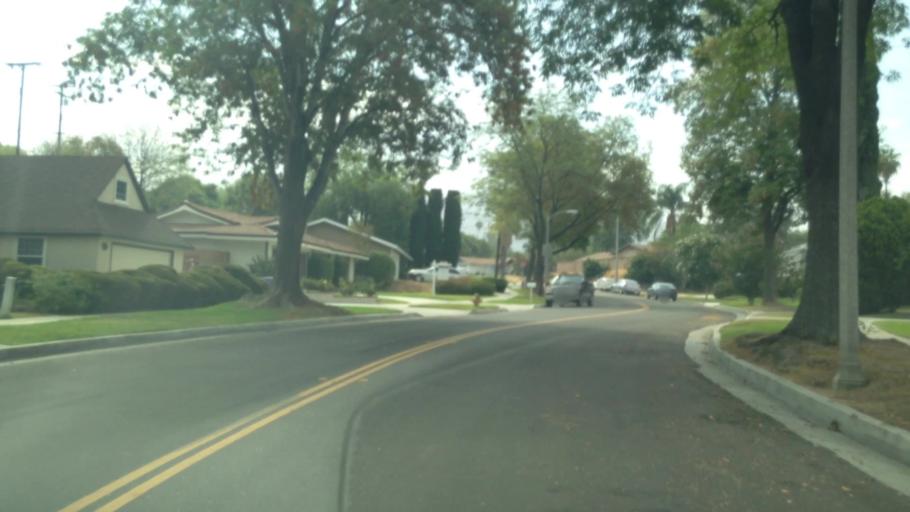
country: US
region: California
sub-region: Riverside County
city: Highgrove
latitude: 33.9887
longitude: -117.3277
